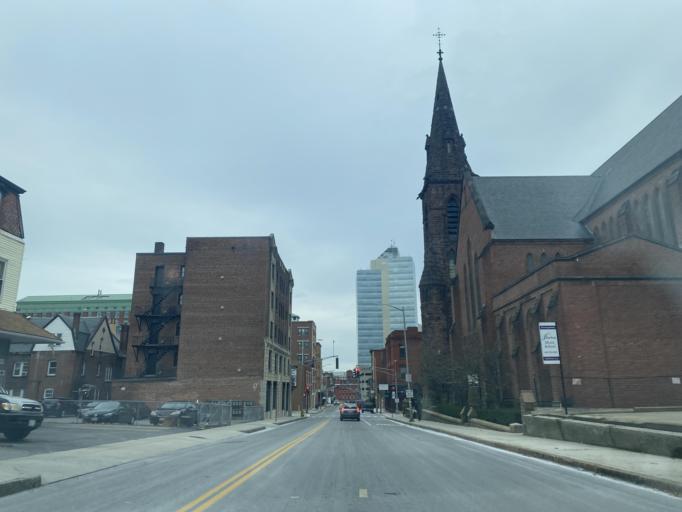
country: US
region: Massachusetts
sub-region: Worcester County
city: Worcester
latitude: 42.2638
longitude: -71.8070
